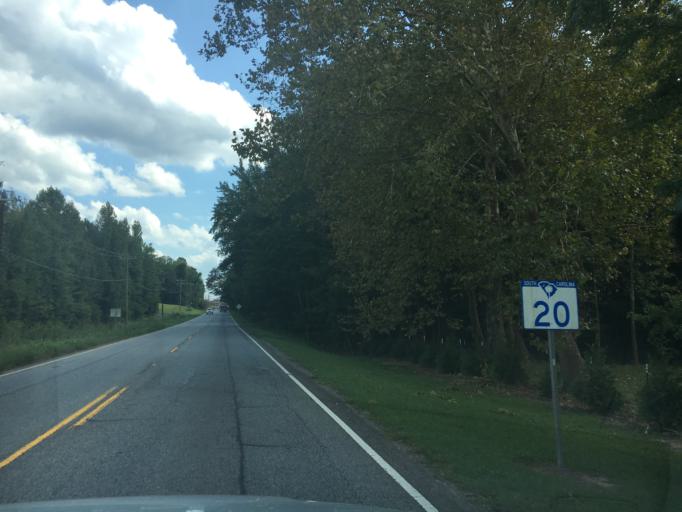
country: US
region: South Carolina
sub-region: Anderson County
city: Belton
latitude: 34.5707
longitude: -82.4926
